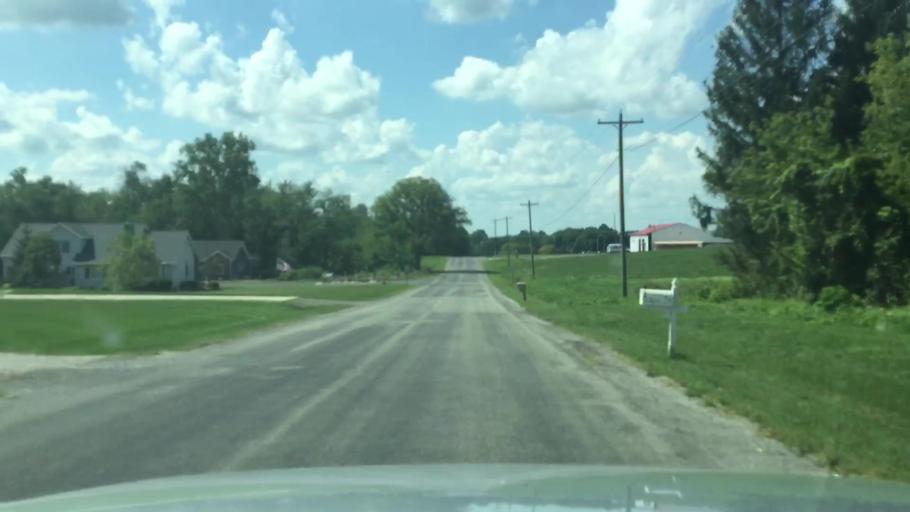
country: US
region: Michigan
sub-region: Lenawee County
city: Clinton
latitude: 42.0724
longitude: -83.9576
